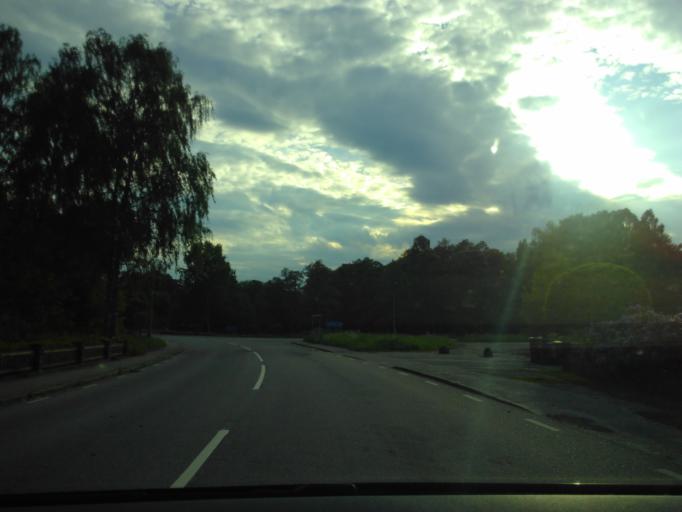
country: SE
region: Vaestra Goetaland
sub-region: Herrljunga Kommun
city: Herrljunga
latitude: 58.0824
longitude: 13.0453
